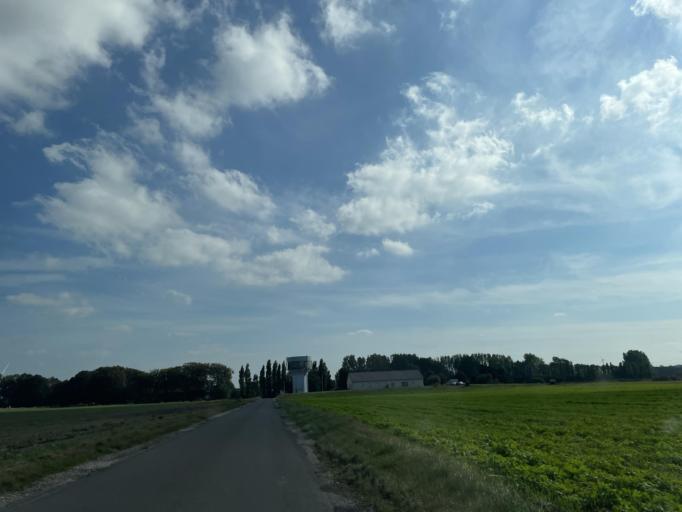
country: FR
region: Haute-Normandie
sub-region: Departement de la Seine-Maritime
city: Criel-sur-Mer
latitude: 50.0315
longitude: 1.3485
